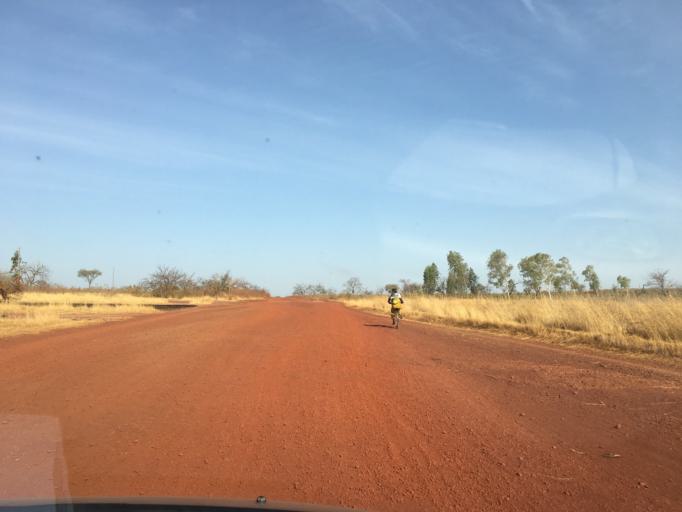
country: BF
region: Plateau-Central
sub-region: Province du Kourweogo
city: Bousse
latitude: 12.5607
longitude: -1.9007
